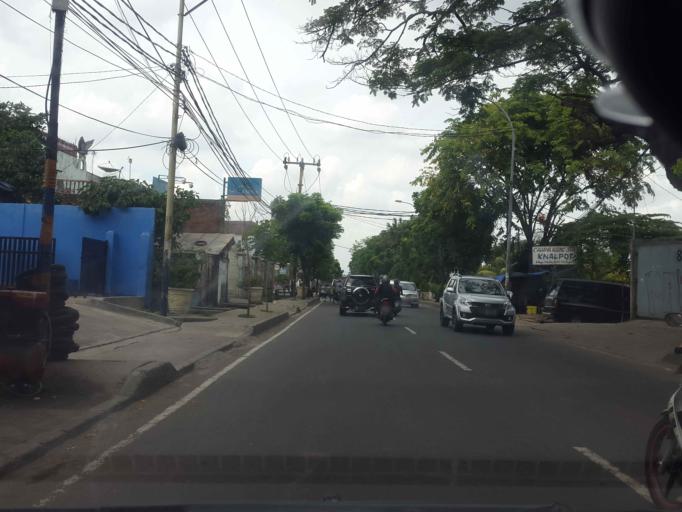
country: ID
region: Banten
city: Tangerang
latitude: -6.1703
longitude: 106.6231
